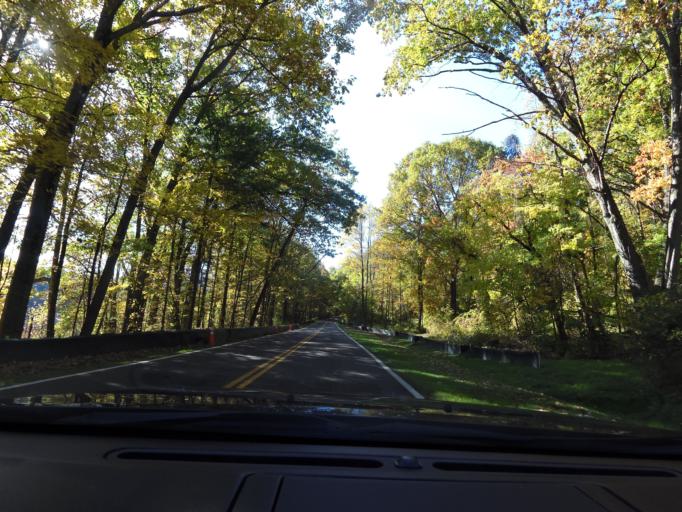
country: US
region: New York
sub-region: Wyoming County
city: Castile
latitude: 42.6108
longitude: -78.0180
